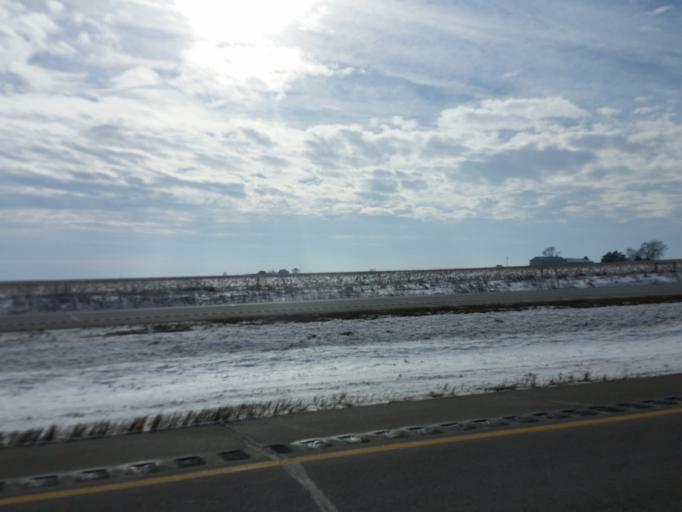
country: US
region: Iowa
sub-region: Buchanan County
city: Independence
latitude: 42.4617
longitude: -91.7465
